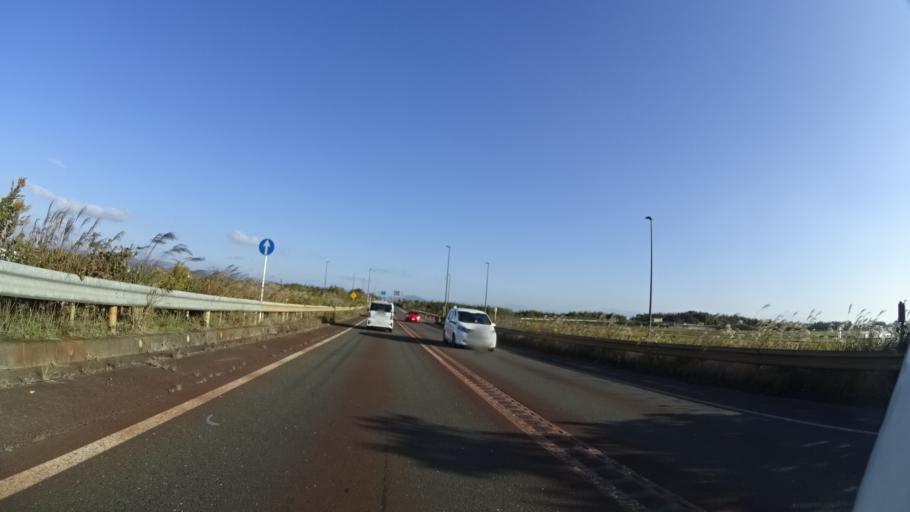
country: JP
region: Shiga Prefecture
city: Kitahama
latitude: 35.3141
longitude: 136.0237
